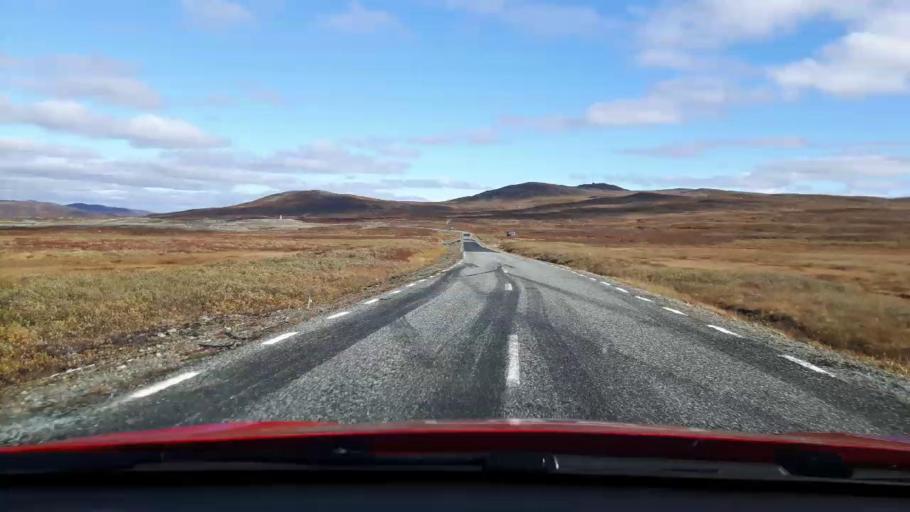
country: NO
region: Nordland
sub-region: Hattfjelldal
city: Hattfjelldal
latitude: 65.0818
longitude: 14.4430
